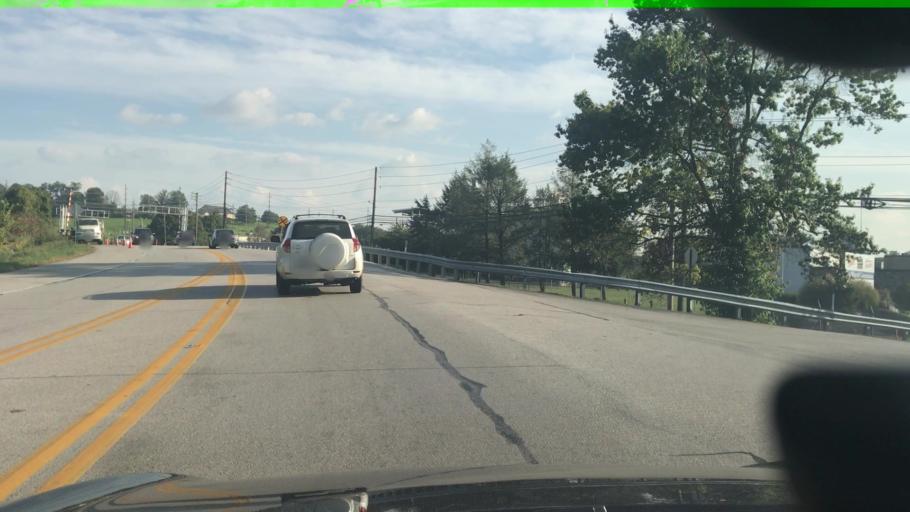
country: US
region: Pennsylvania
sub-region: Cumberland County
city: Shiremanstown
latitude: 40.2112
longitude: -76.9448
